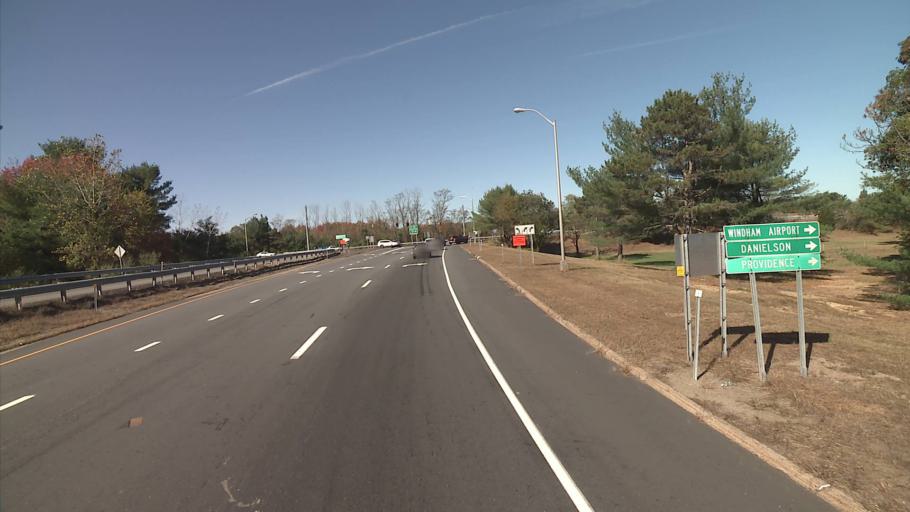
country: US
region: Connecticut
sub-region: Windham County
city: Willimantic
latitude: 41.7333
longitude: -72.1827
